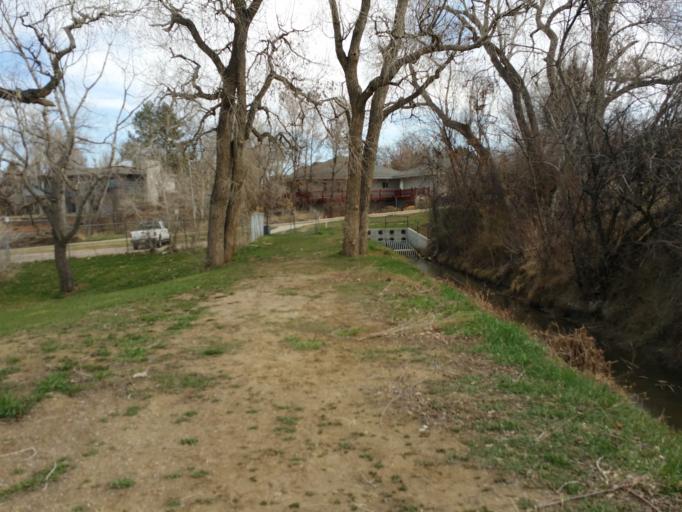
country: US
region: Colorado
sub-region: Jefferson County
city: Wheat Ridge
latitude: 39.7648
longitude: -105.1029
